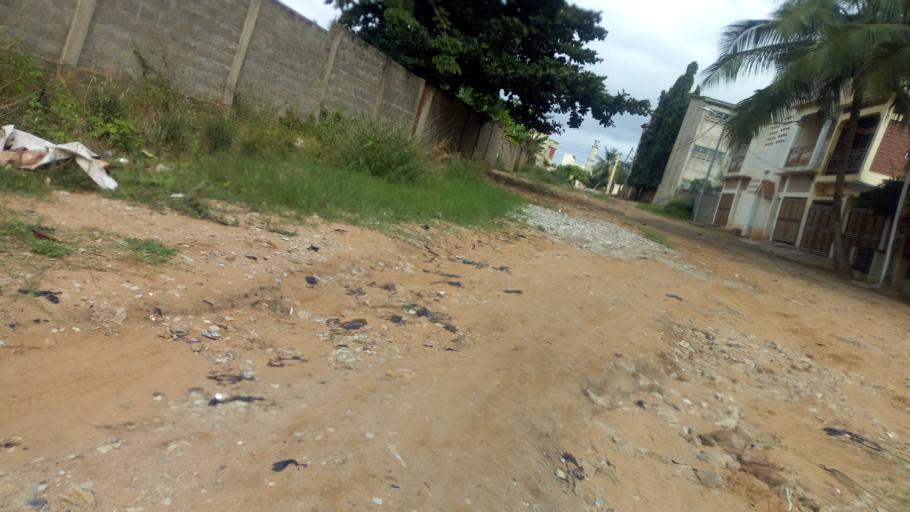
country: TG
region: Maritime
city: Lome
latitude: 6.1744
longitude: 1.1755
